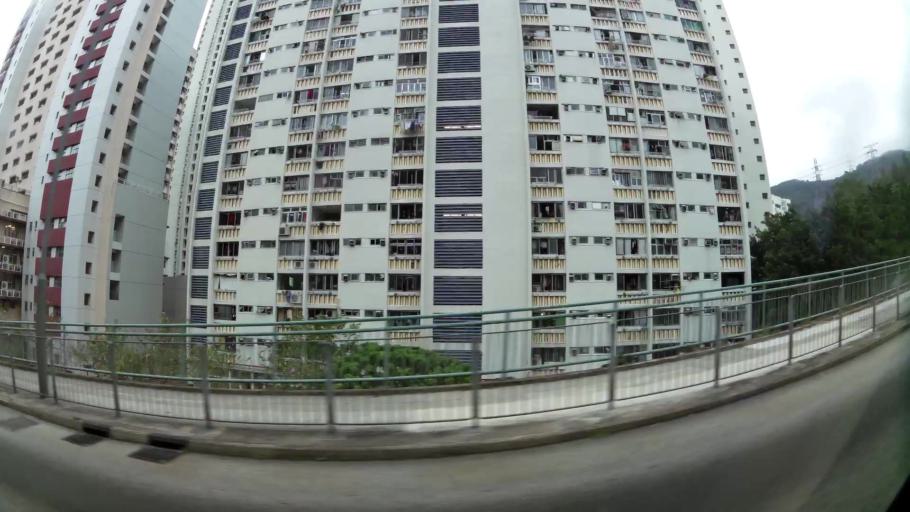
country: HK
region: Tsuen Wan
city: Tsuen Wan
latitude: 22.3794
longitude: 114.1373
